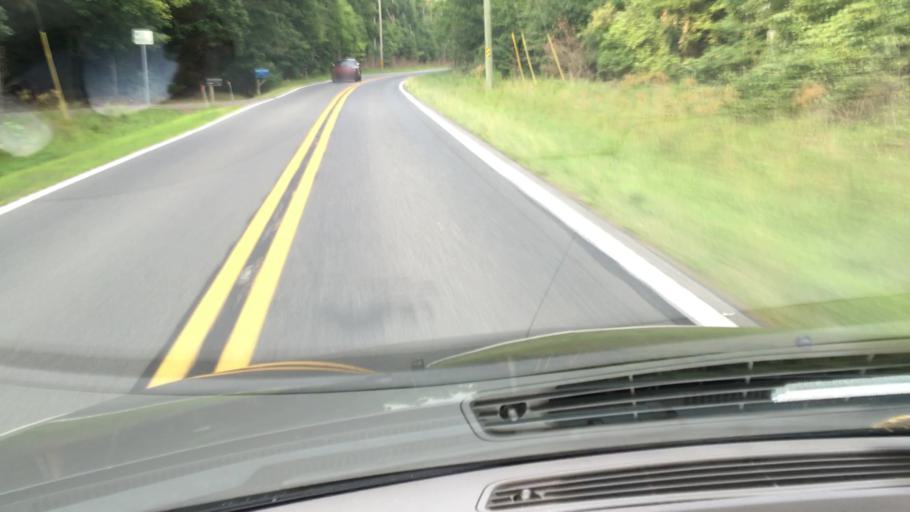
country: US
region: Delaware
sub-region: Sussex County
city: Ocean View
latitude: 38.5086
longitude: -75.1131
